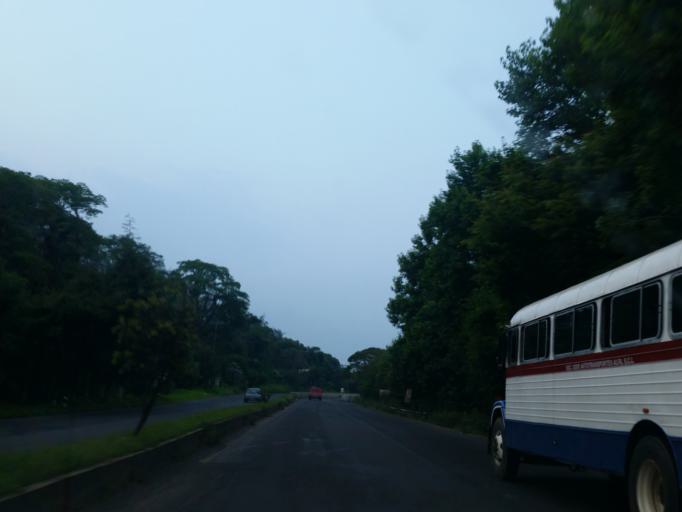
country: MX
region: Veracruz
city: Coatepec
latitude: 19.4746
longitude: -96.9437
